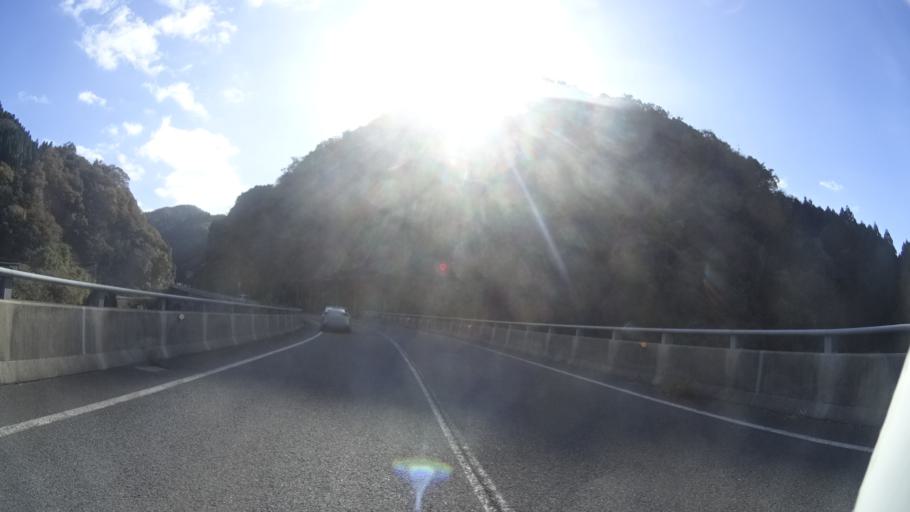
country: JP
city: Asahi
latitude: 35.9600
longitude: 135.9959
